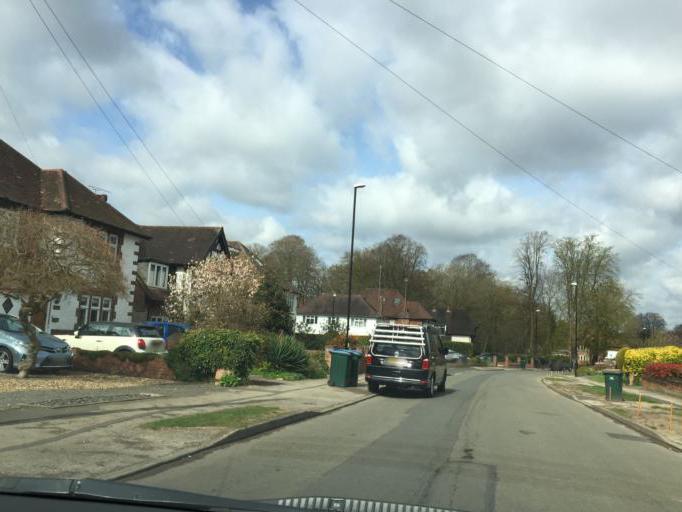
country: GB
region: England
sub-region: Coventry
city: Coventry
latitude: 52.3867
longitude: -1.5185
